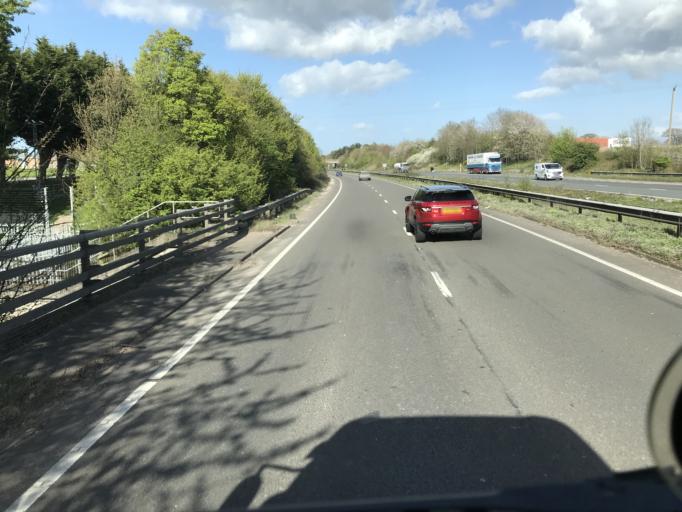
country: GB
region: England
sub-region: Cheshire West and Chester
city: Eccleston
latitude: 53.1684
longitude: -2.8664
